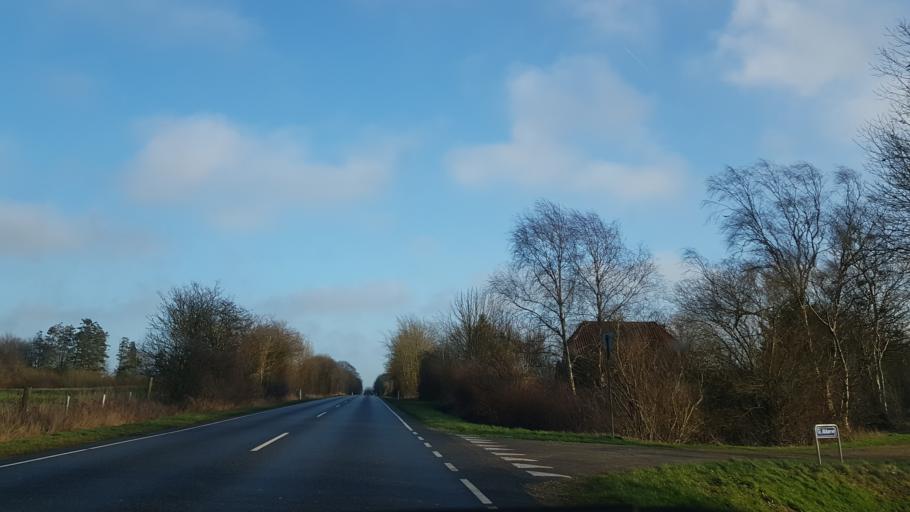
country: DK
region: South Denmark
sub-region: Haderslev Kommune
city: Vojens
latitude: 55.1719
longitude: 9.3582
